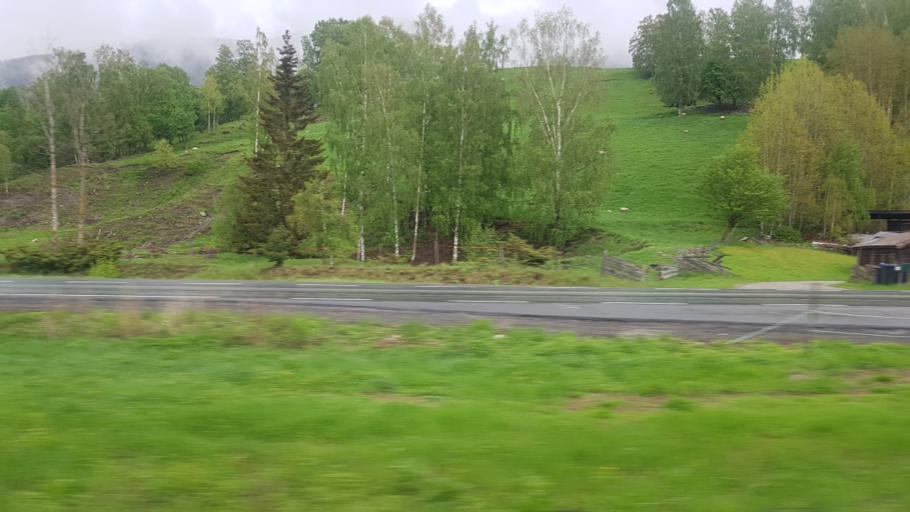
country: NO
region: Oppland
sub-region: Ringebu
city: Ringebu
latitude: 61.5471
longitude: 10.0578
